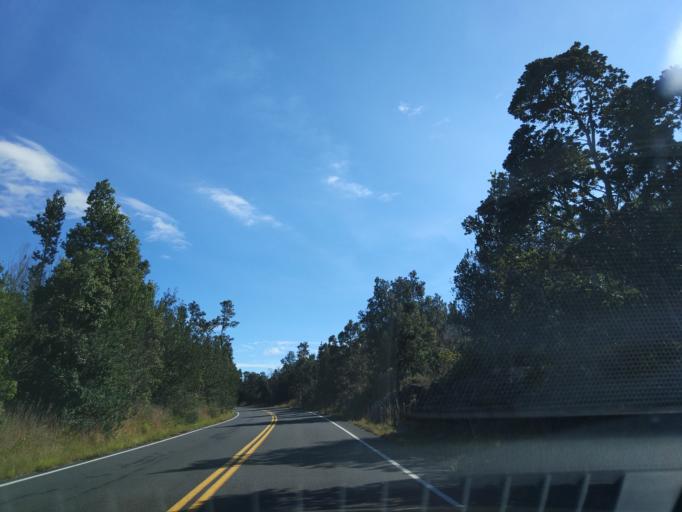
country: US
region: Hawaii
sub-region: Hawaii County
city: Volcano
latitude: 19.3495
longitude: -155.2189
